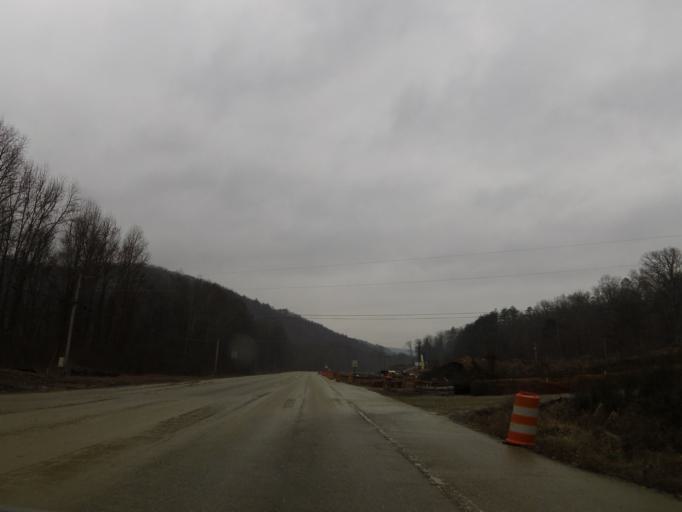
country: US
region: Tennessee
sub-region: Morgan County
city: Coalfield
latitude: 35.9917
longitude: -84.4928
